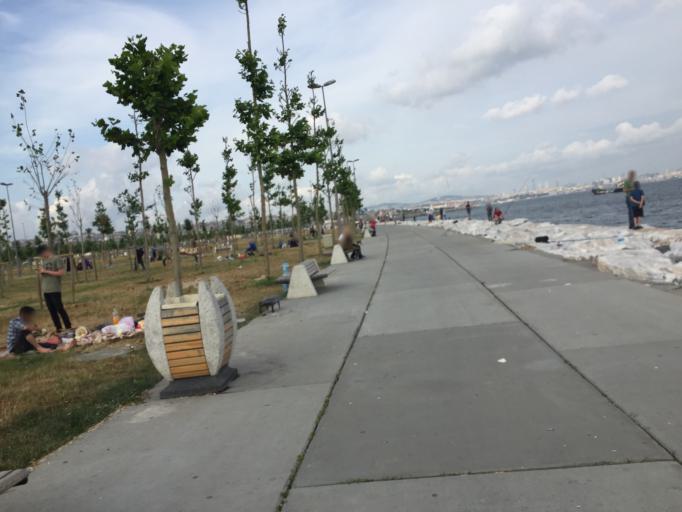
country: TR
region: Istanbul
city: Istanbul
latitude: 40.9966
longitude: 28.9492
